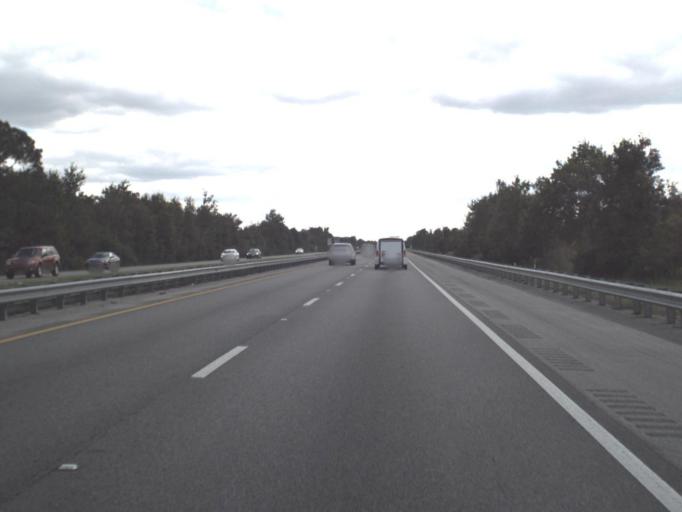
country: US
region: Florida
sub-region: Osceola County
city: Saint Cloud
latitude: 28.1430
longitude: -81.2942
